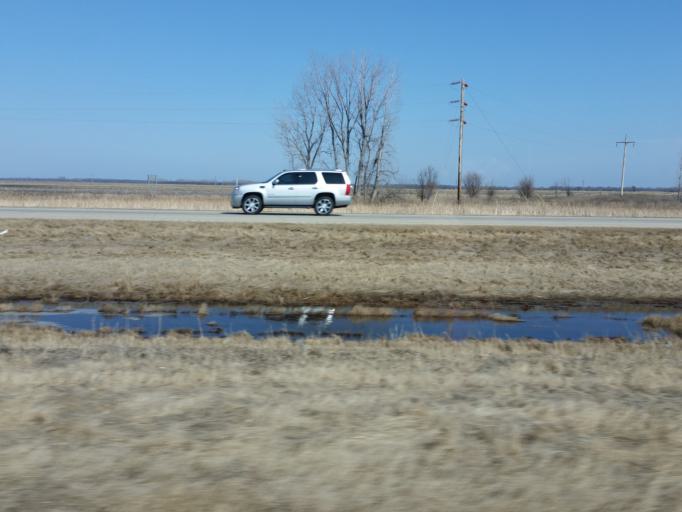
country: US
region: North Dakota
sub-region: Grand Forks County
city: Grand Forks
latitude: 48.0193
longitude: -97.1247
